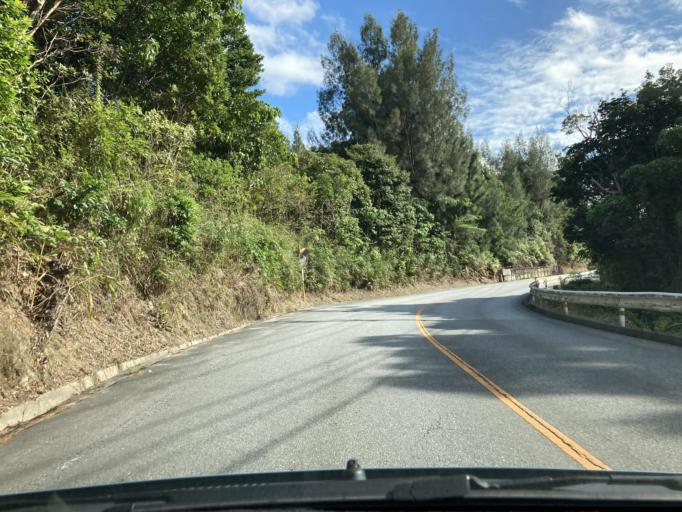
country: JP
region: Okinawa
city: Ishikawa
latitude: 26.4360
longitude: 127.8066
